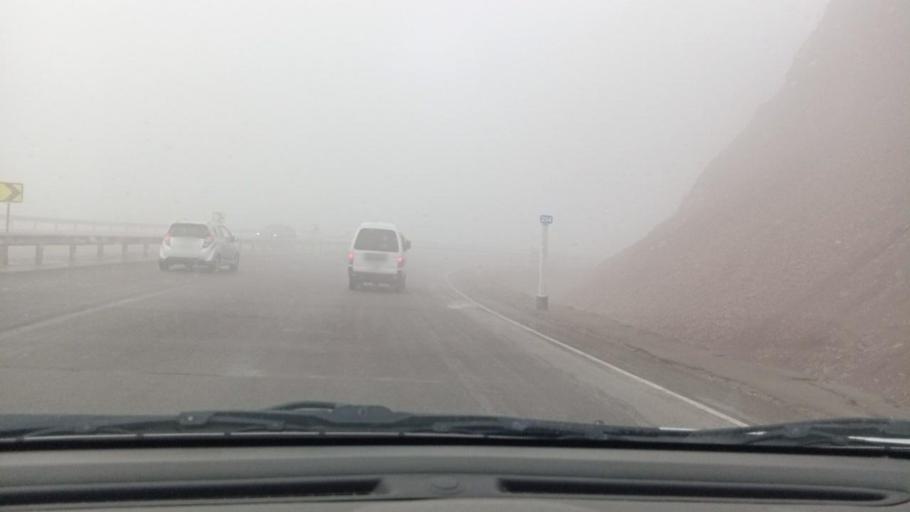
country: UZ
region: Toshkent
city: Angren
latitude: 41.1093
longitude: 70.5055
